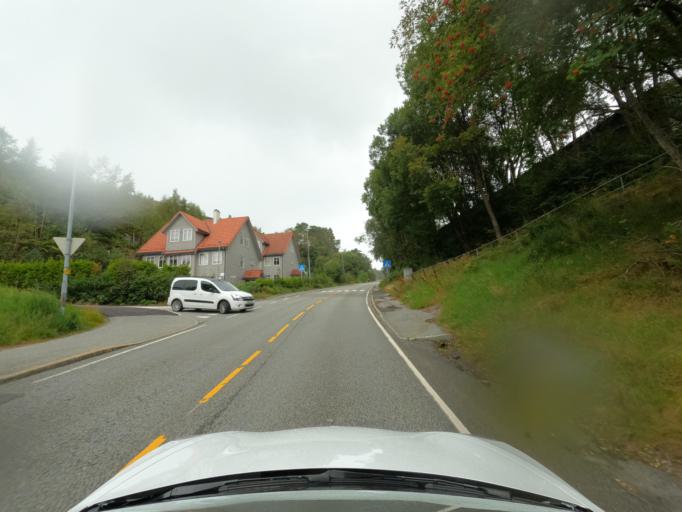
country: NO
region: Hordaland
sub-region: Bergen
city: Hylkje
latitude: 60.4693
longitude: 5.3047
